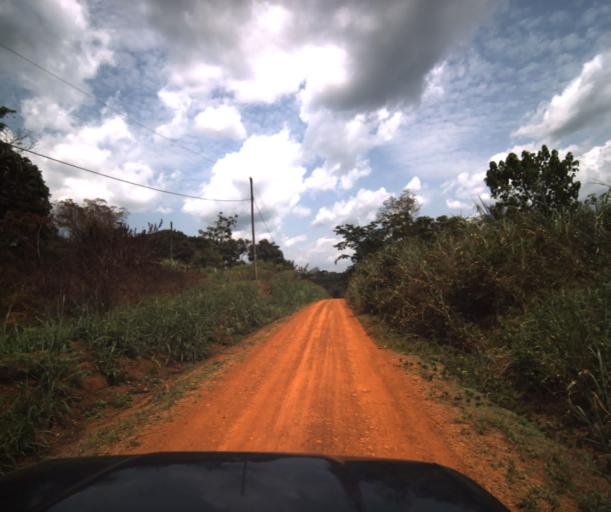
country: CM
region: Centre
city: Eseka
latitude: 3.5493
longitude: 10.9250
